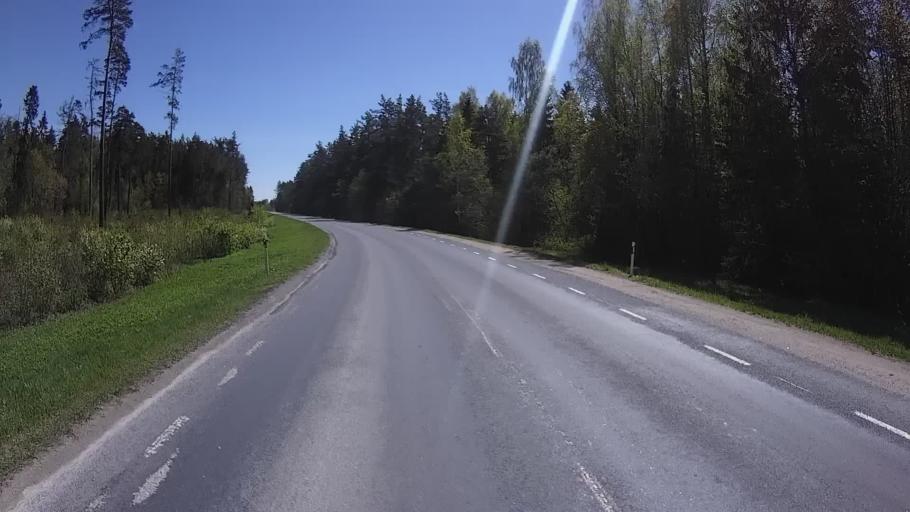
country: EE
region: Harju
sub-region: Raasiku vald
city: Raasiku
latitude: 59.1641
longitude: 25.1782
